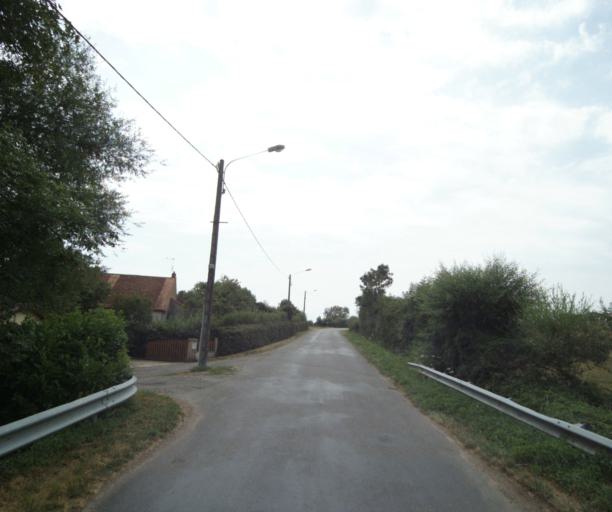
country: FR
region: Bourgogne
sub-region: Departement de Saone-et-Loire
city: Gueugnon
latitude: 46.5921
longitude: 4.0415
